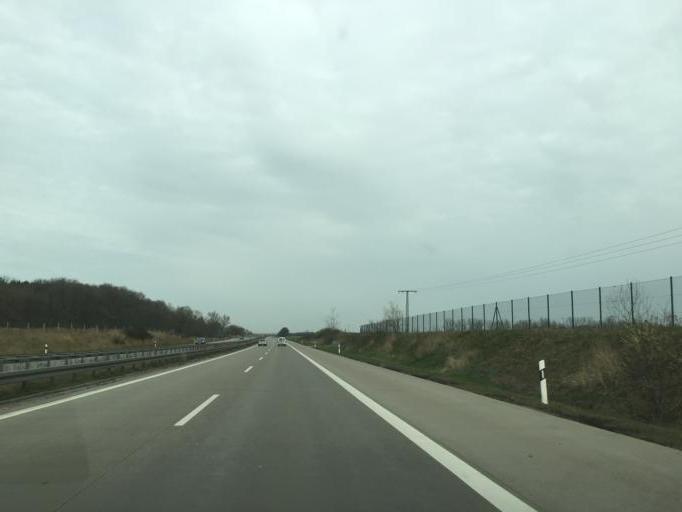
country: DE
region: Mecklenburg-Vorpommern
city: Laage
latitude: 53.8989
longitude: 12.2515
